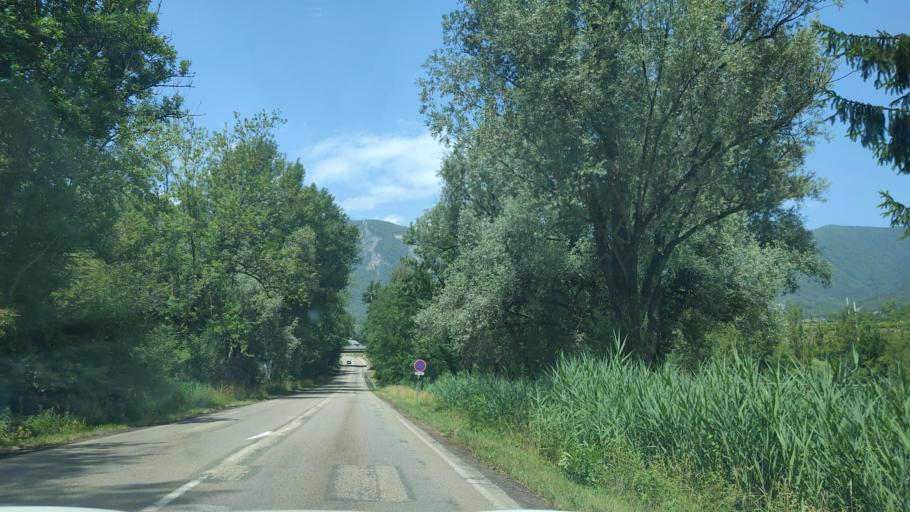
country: FR
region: Rhone-Alpes
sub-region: Departement de la Savoie
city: Coise-Saint-Jean-Pied-Gauthier
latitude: 45.5571
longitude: 6.1646
